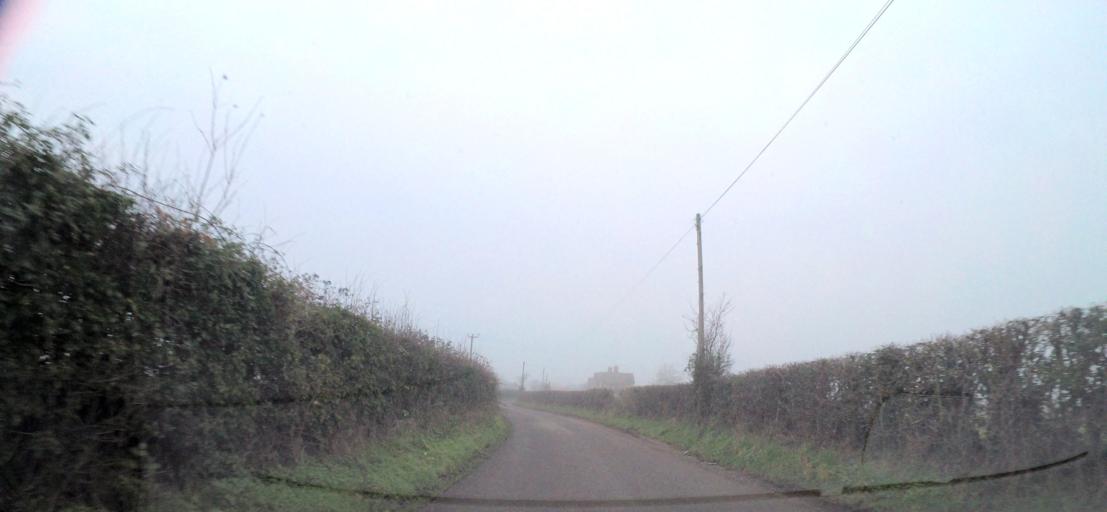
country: GB
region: England
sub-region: West Berkshire
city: Theale
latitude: 51.4075
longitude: -1.0986
